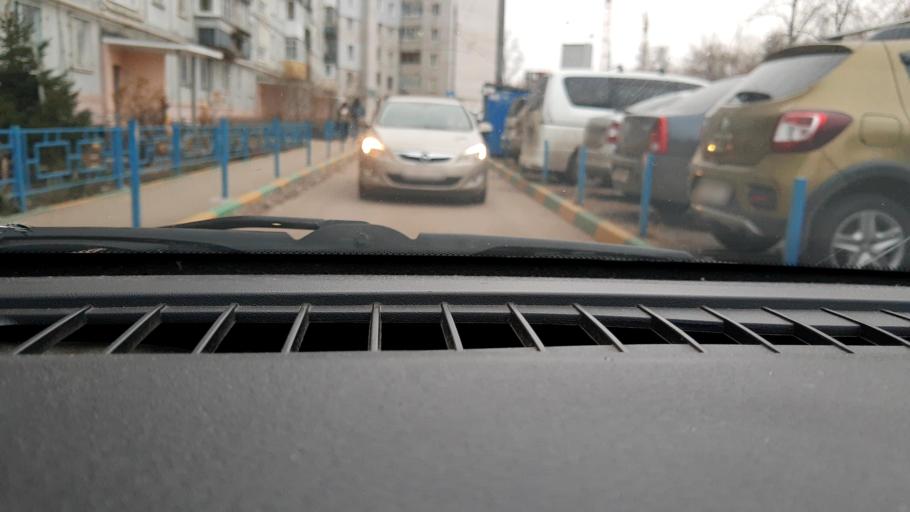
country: RU
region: Nizjnij Novgorod
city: Nizhniy Novgorod
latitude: 56.2787
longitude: 43.9452
